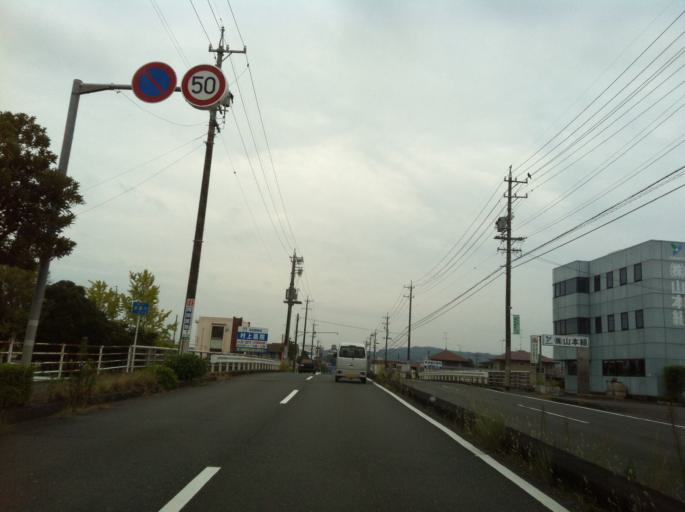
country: JP
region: Shizuoka
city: Kakegawa
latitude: 34.7848
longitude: 138.0131
